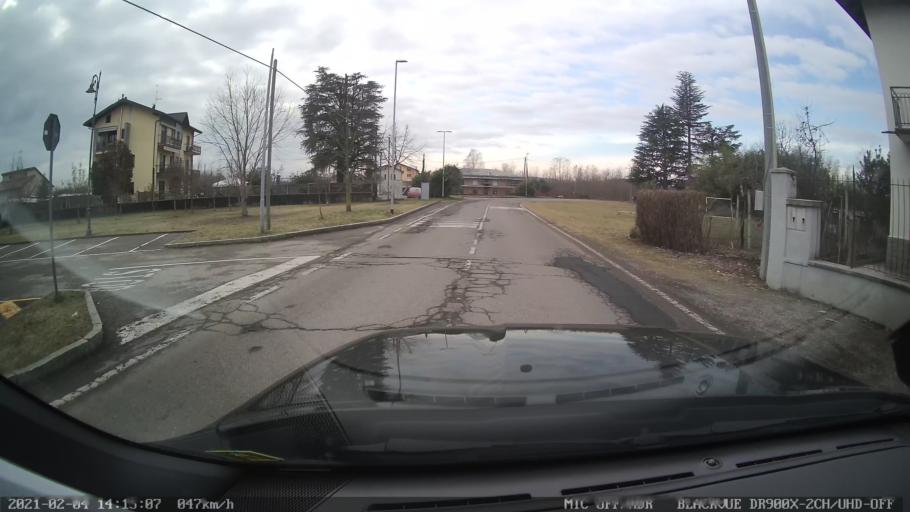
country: IT
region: Lombardy
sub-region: Provincia di Varese
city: Lonate Ceppino
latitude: 45.7221
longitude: 8.8873
